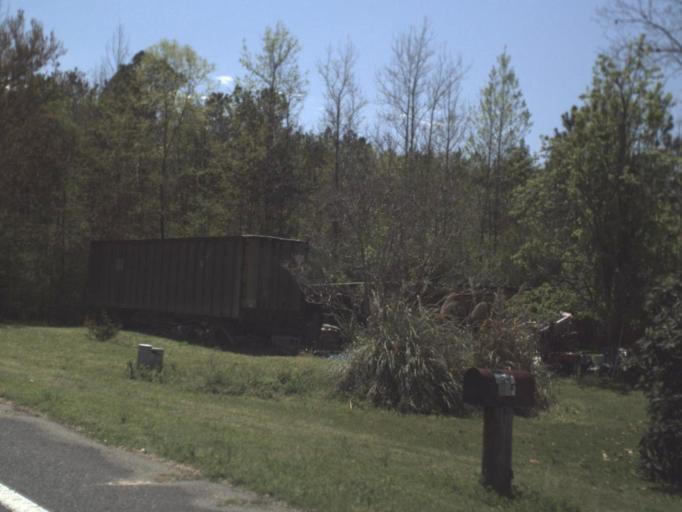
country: US
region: Alabama
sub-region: Geneva County
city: Geneva
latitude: 30.9681
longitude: -85.9981
